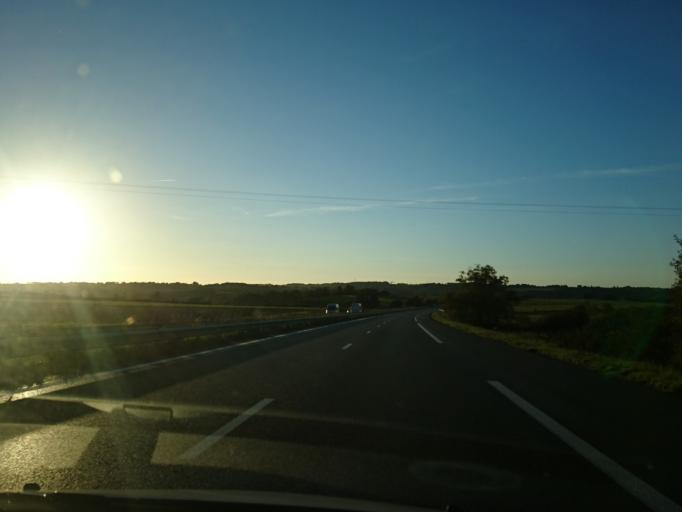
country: FR
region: Brittany
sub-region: Departement du Finistere
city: Guerlesquin
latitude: 48.5711
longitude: -3.6221
